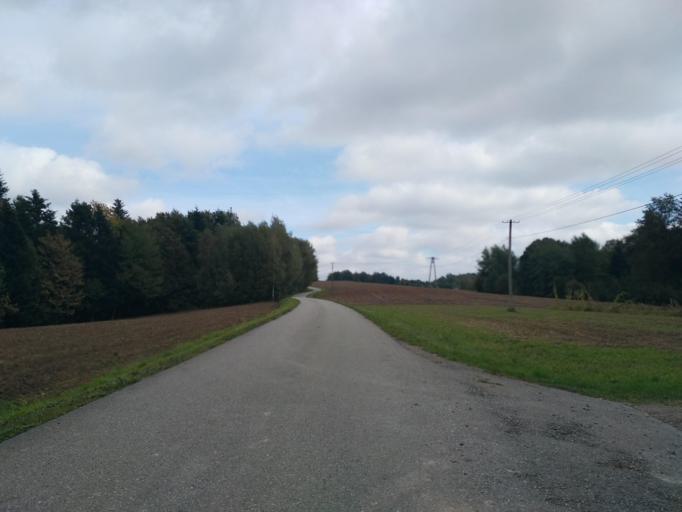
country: PL
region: Subcarpathian Voivodeship
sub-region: Powiat ropczycko-sedziszowski
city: Niedzwiada
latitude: 49.9203
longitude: 21.4969
